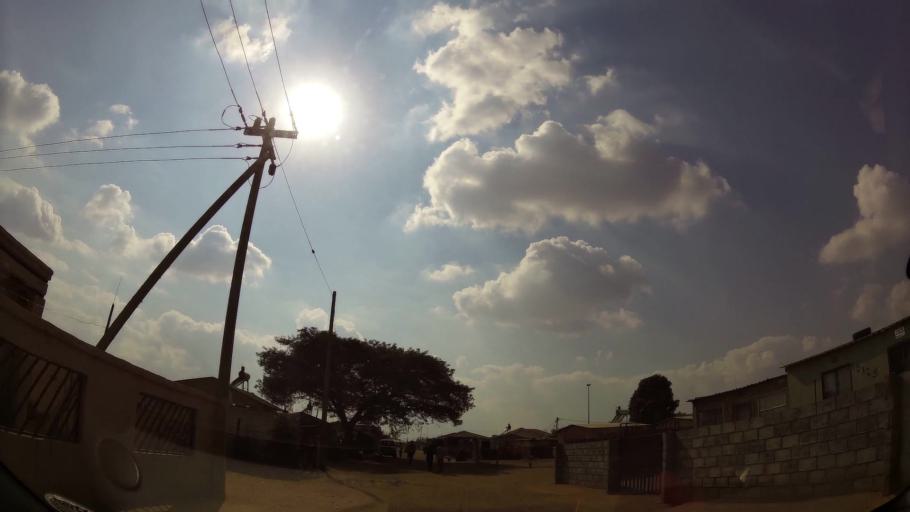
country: ZA
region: Gauteng
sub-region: Ekurhuleni Metropolitan Municipality
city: Springs
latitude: -26.1218
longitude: 28.4796
